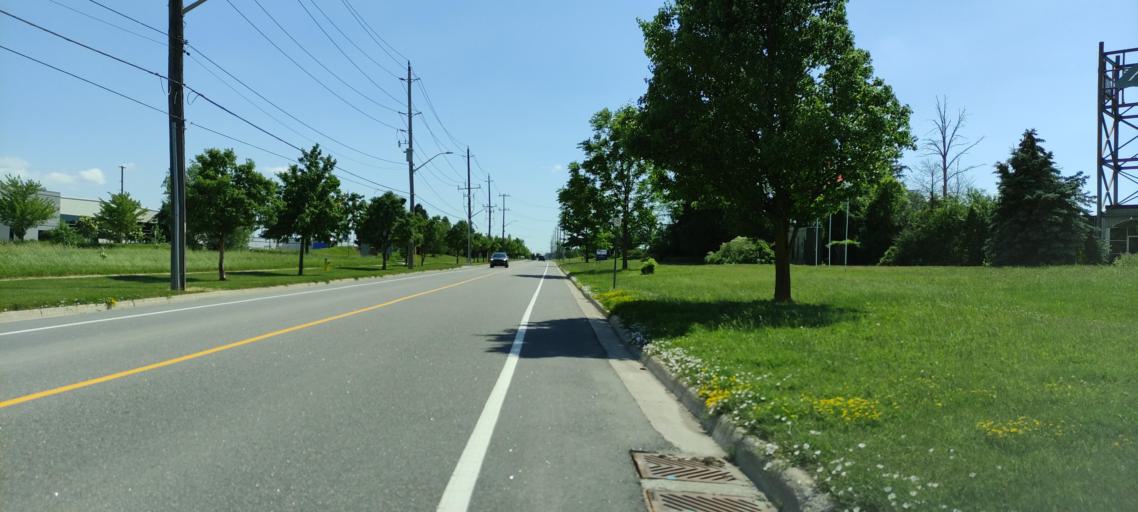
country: CA
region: Ontario
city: Stratford
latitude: 43.3581
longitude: -81.0089
